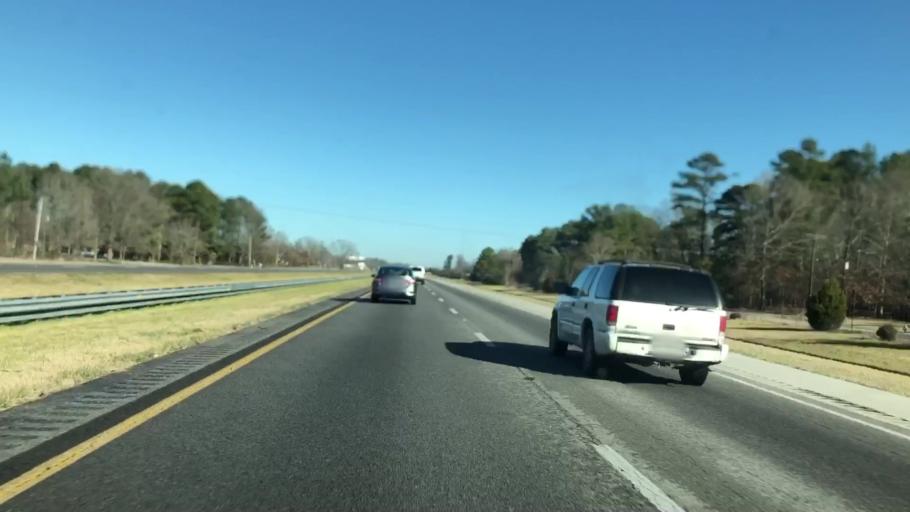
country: US
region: Alabama
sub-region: Limestone County
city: Athens
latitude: 34.8689
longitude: -86.9234
